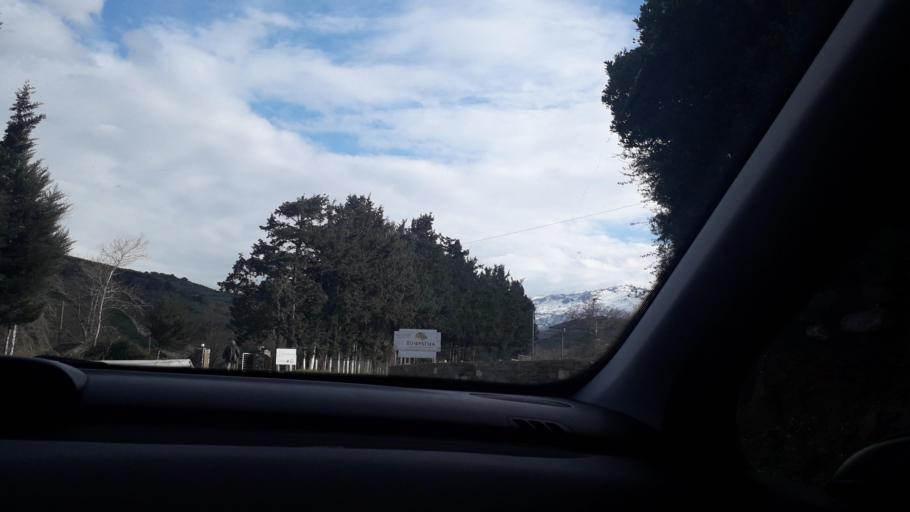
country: GR
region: Crete
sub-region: Nomos Rethymnis
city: Agia Foteini
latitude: 35.2920
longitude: 24.5593
